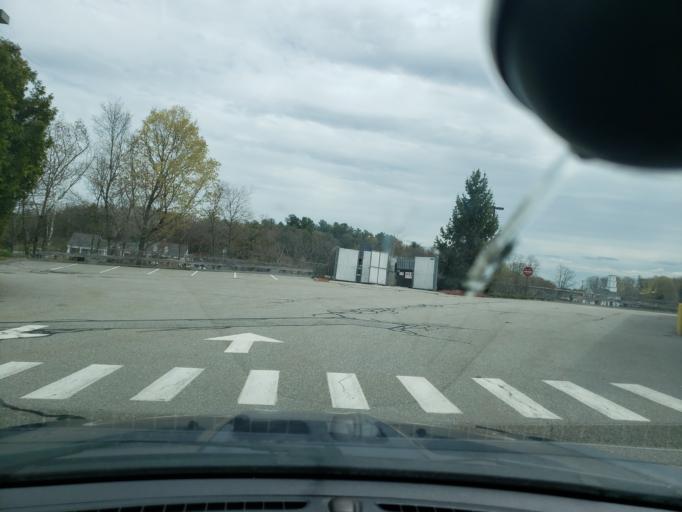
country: US
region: Connecticut
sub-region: Hartford County
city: Collinsville
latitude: 41.7709
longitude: -72.9697
